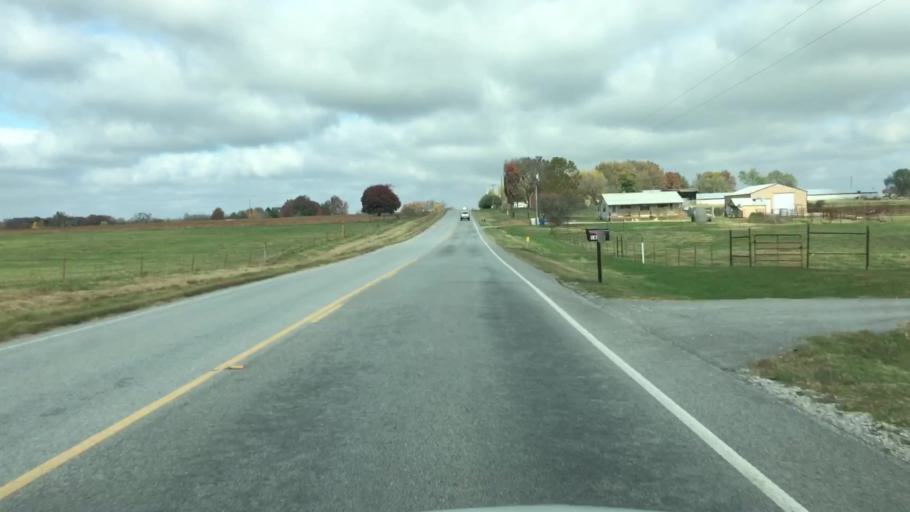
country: US
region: Arkansas
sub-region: Benton County
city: Centerton
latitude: 36.2763
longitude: -94.3502
